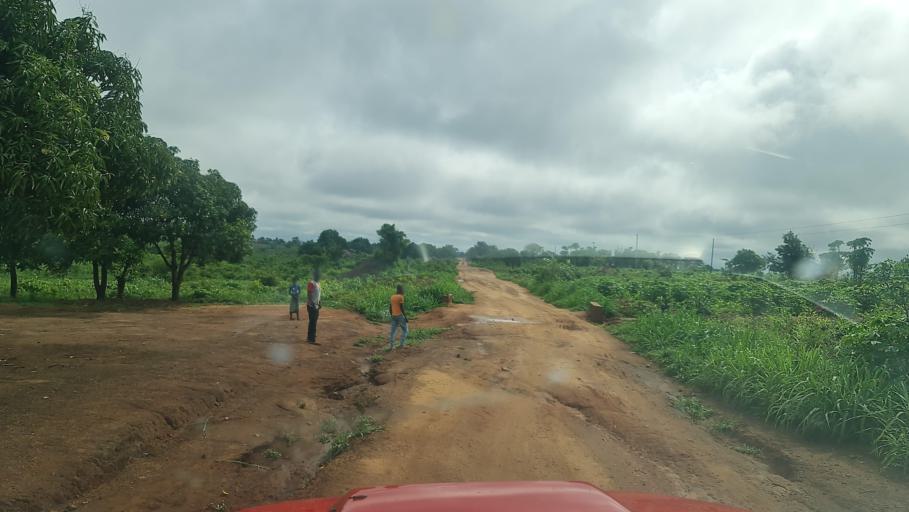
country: MW
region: Southern Region
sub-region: Nsanje District
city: Nsanje
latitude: -17.2223
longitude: 35.6667
